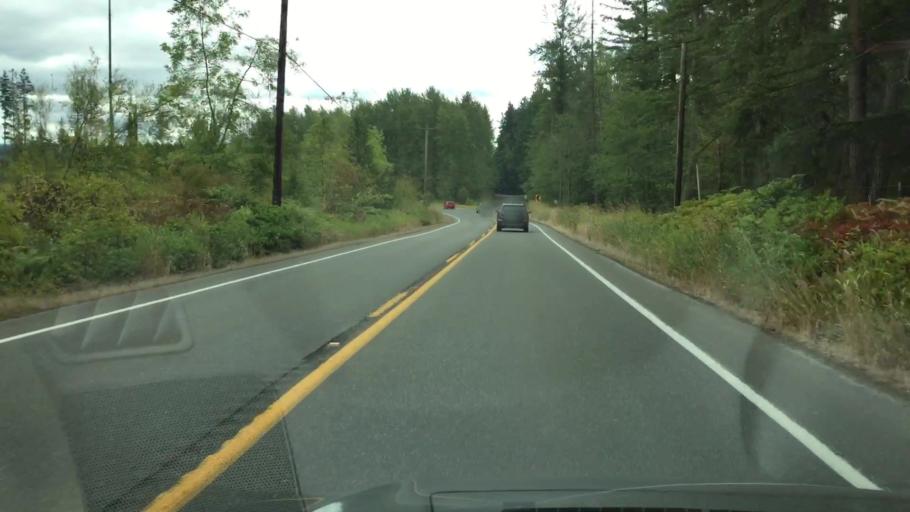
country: US
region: Washington
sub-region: Pierce County
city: Eatonville
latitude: 46.9546
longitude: -122.2972
